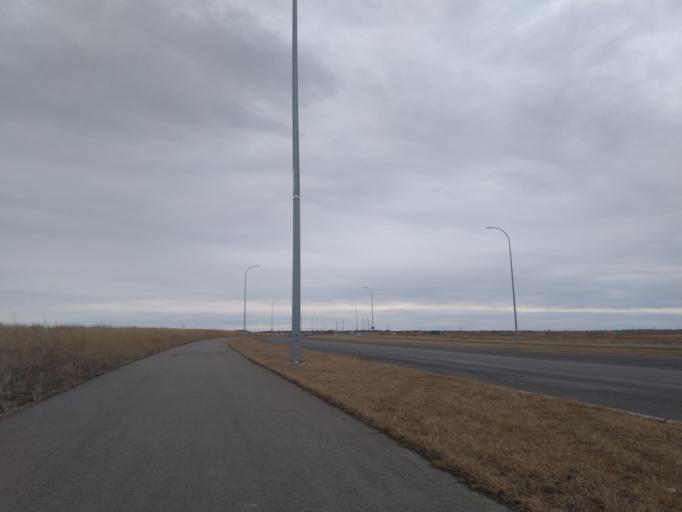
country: CA
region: Alberta
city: Airdrie
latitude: 51.1689
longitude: -113.9879
